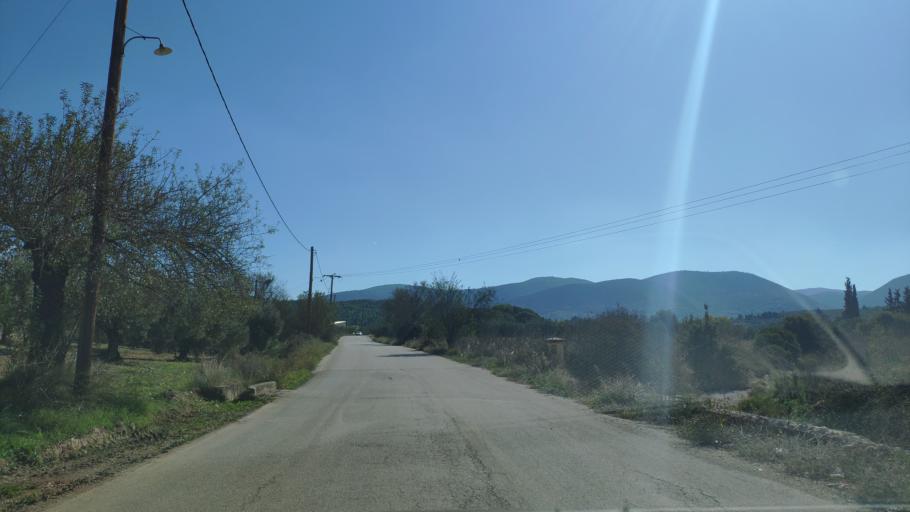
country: GR
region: Peloponnese
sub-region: Nomos Korinthias
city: Athikia
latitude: 37.8400
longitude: 22.9098
